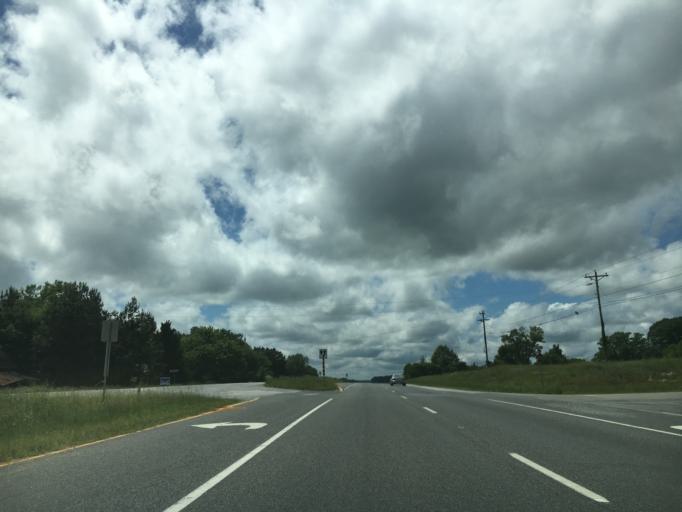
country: US
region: Virginia
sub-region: Mecklenburg County
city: Boydton
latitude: 36.6714
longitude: -78.2580
